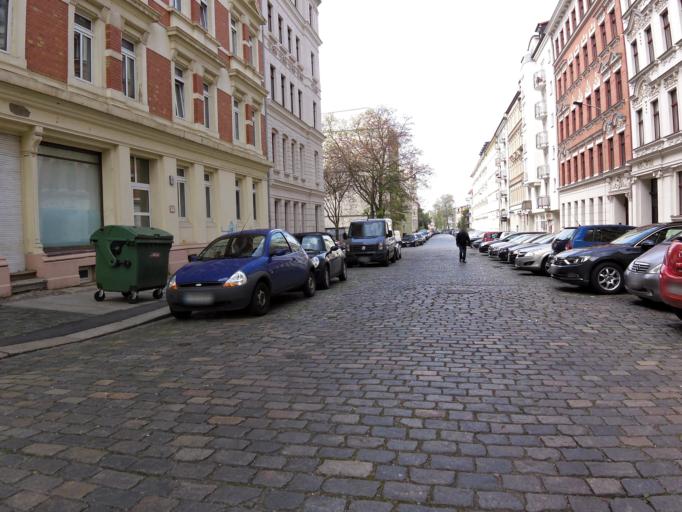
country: DE
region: Saxony
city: Leipzig
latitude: 51.3588
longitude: 12.3779
